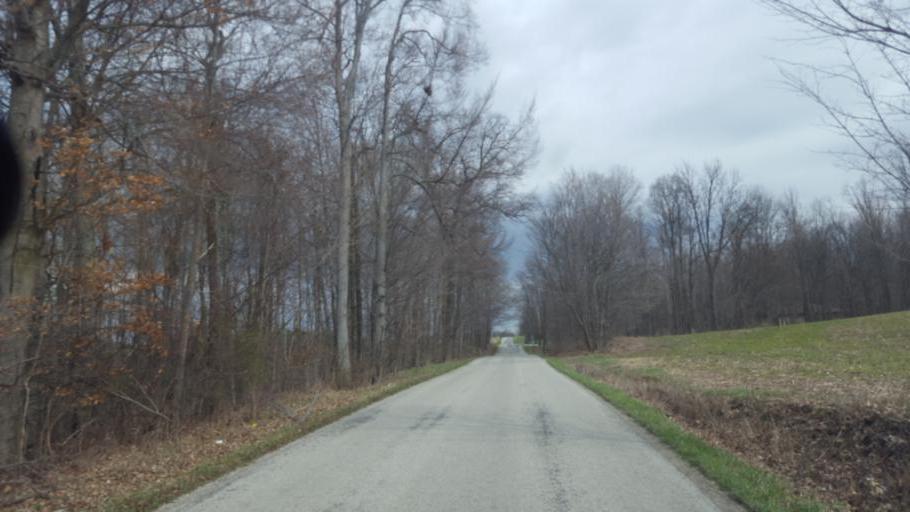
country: US
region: Ohio
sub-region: Morrow County
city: Mount Gilead
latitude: 40.5504
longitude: -82.7584
